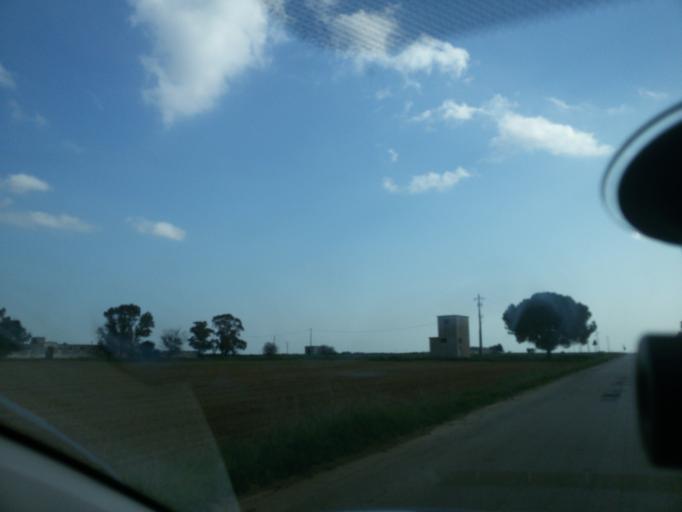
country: IT
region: Apulia
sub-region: Provincia di Brindisi
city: Mesagne
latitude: 40.6456
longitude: 17.8154
